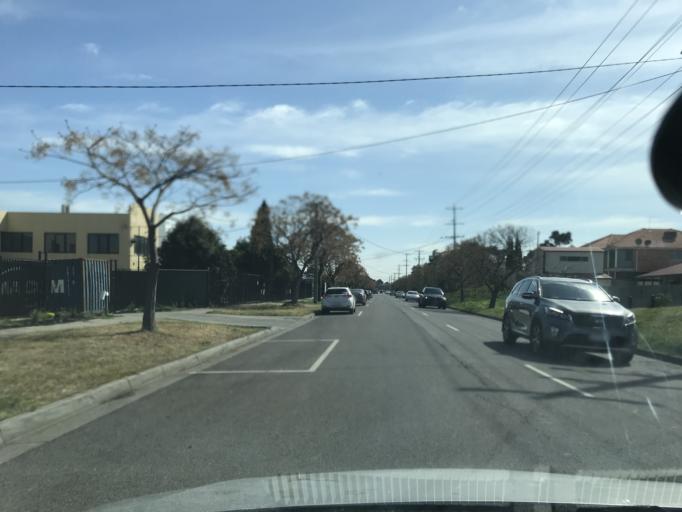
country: AU
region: Victoria
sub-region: Whittlesea
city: Epping
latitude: -37.6429
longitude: 145.0207
